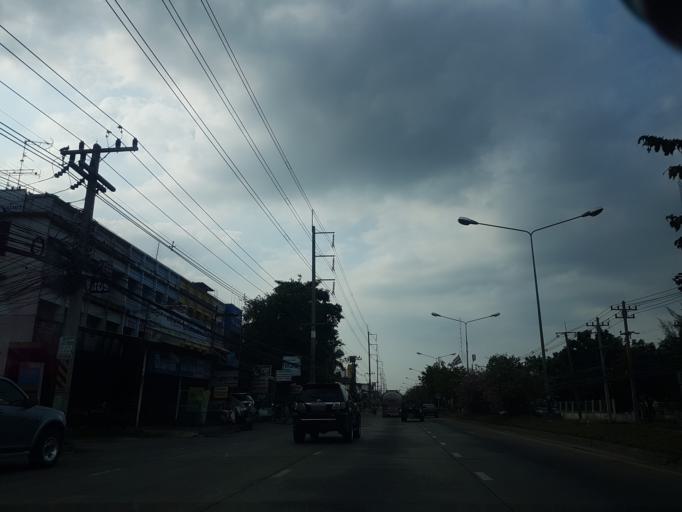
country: TH
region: Sara Buri
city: Phra Phutthabat
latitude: 14.7275
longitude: 100.7925
